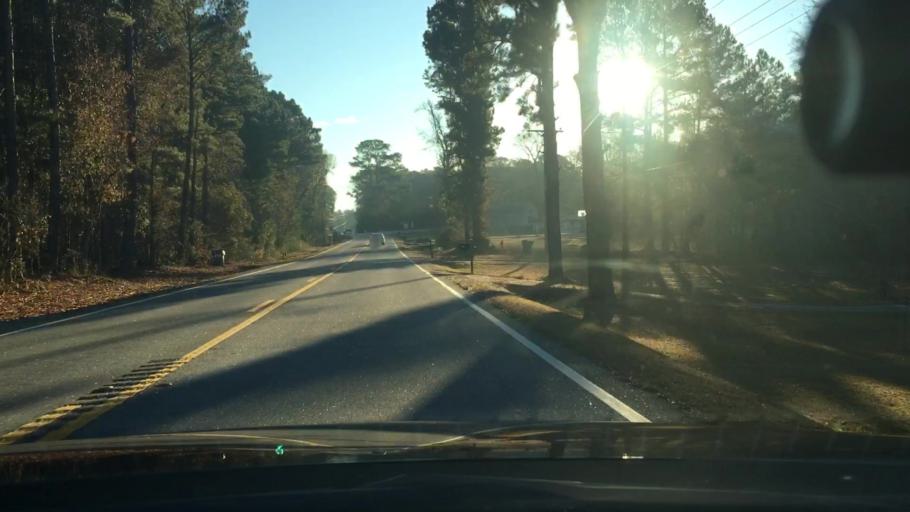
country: US
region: Georgia
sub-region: Fayette County
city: Peachtree City
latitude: 33.3432
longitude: -84.6518
